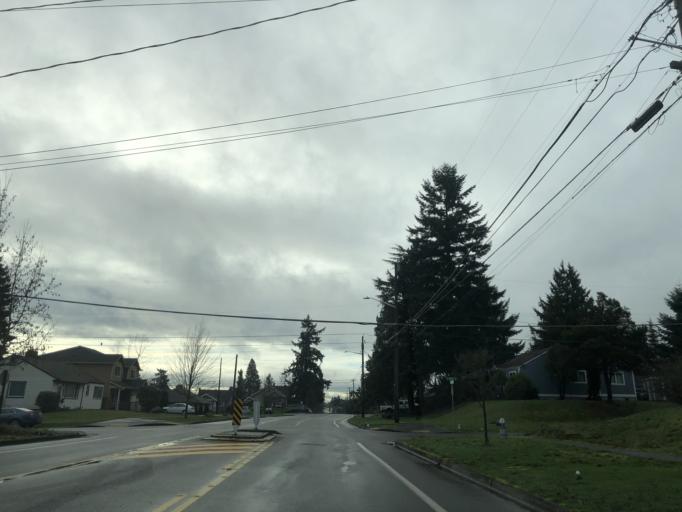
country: US
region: Washington
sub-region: Pierce County
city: Tacoma
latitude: 47.2224
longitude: -122.4580
